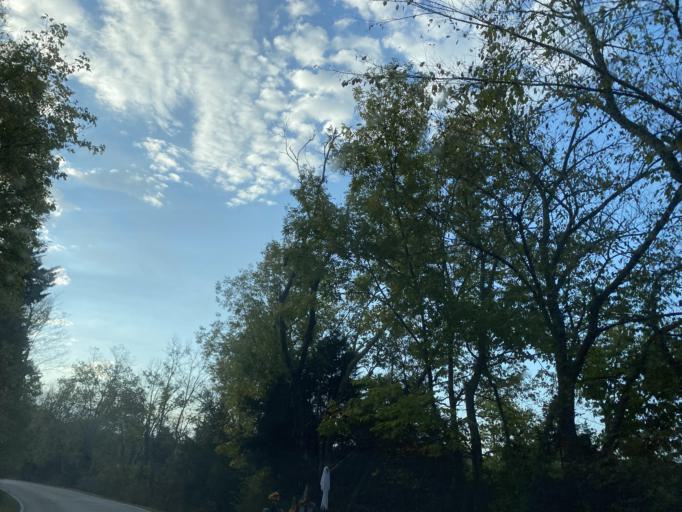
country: US
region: Kentucky
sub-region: Pendleton County
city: Falmouth
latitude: 38.7598
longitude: -84.3413
